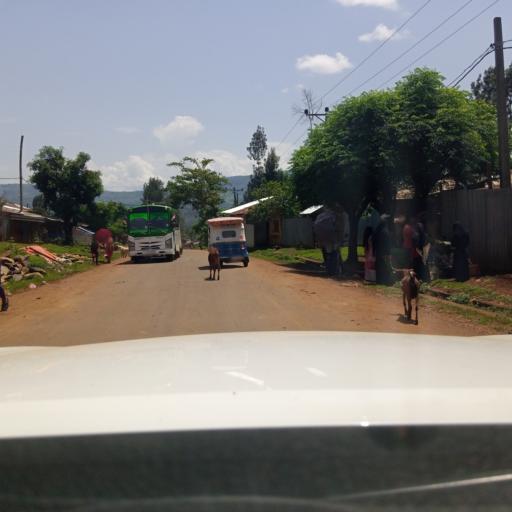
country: ET
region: Oromiya
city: Agaro
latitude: 8.0955
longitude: 36.9457
